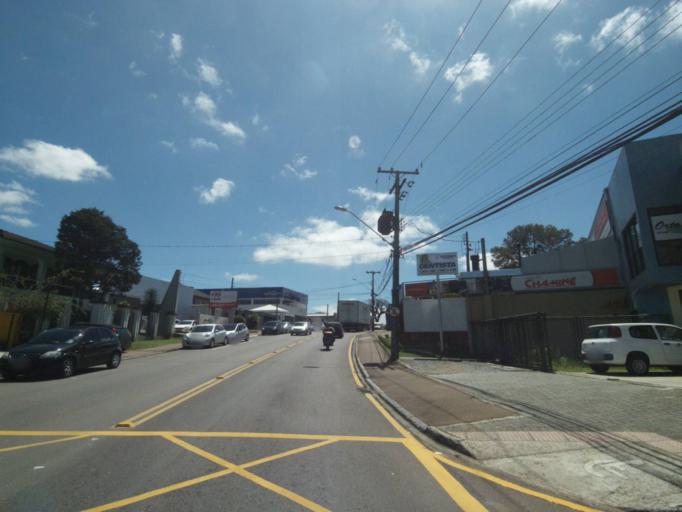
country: BR
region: Parana
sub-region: Curitiba
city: Curitiba
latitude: -25.3829
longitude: -49.2617
